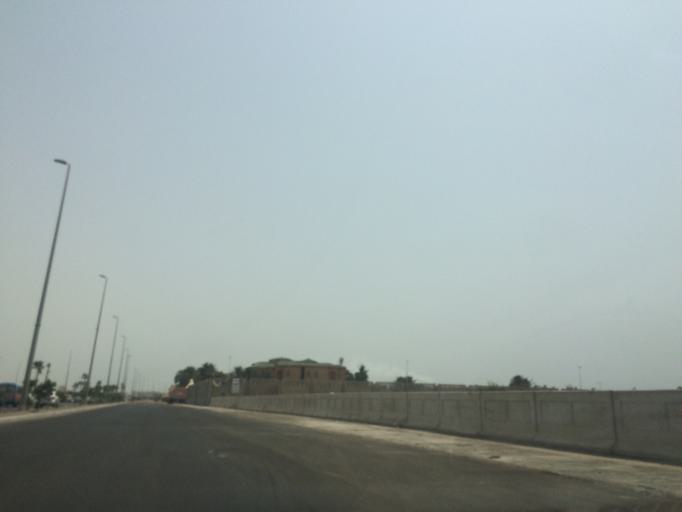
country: SA
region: Makkah
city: Jeddah
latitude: 21.5877
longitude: 39.1249
